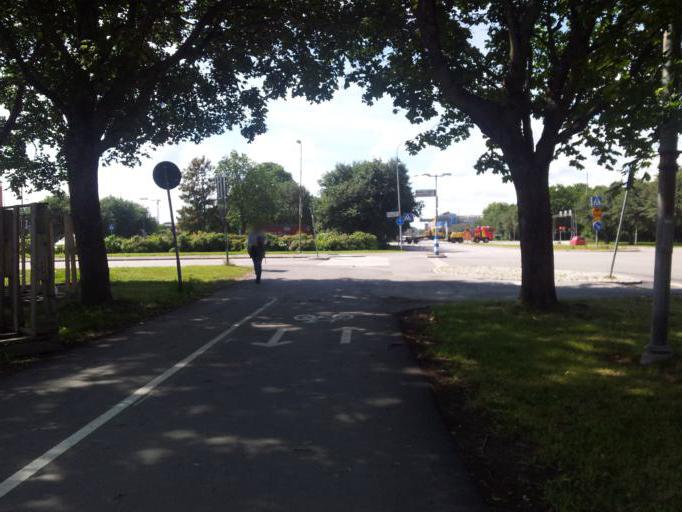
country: SE
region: Uppsala
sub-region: Uppsala Kommun
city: Uppsala
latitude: 59.8732
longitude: 17.6528
